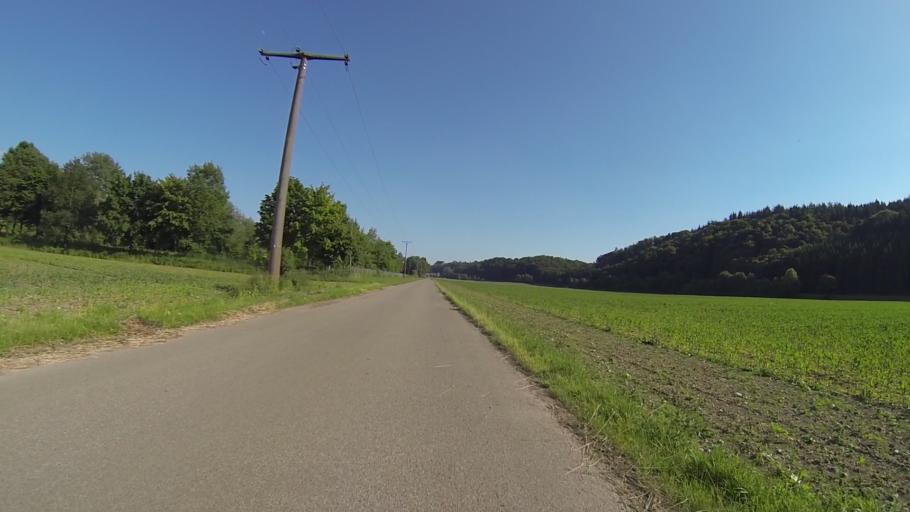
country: DE
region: Baden-Wuerttemberg
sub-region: Tuebingen Region
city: Warthausen
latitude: 48.1468
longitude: 9.7931
